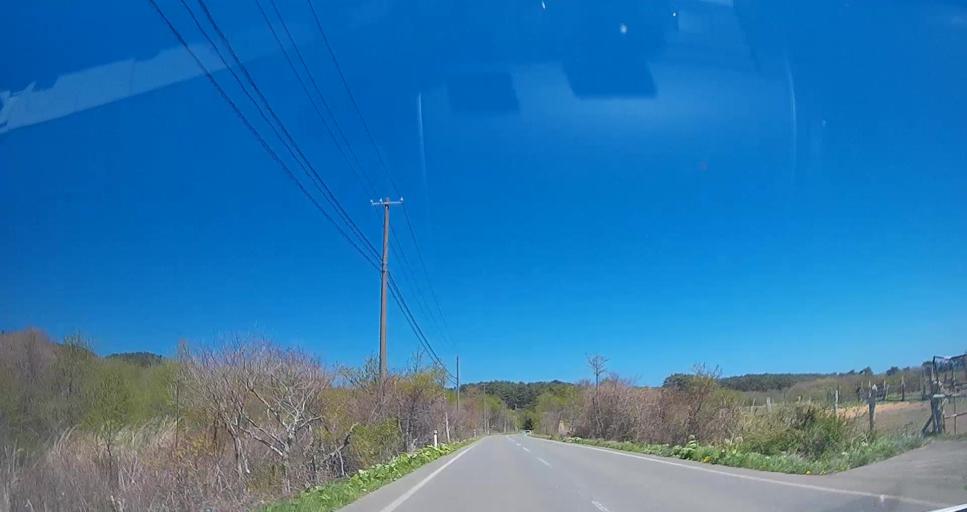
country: JP
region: Aomori
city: Mutsu
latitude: 41.2570
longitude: 141.3892
